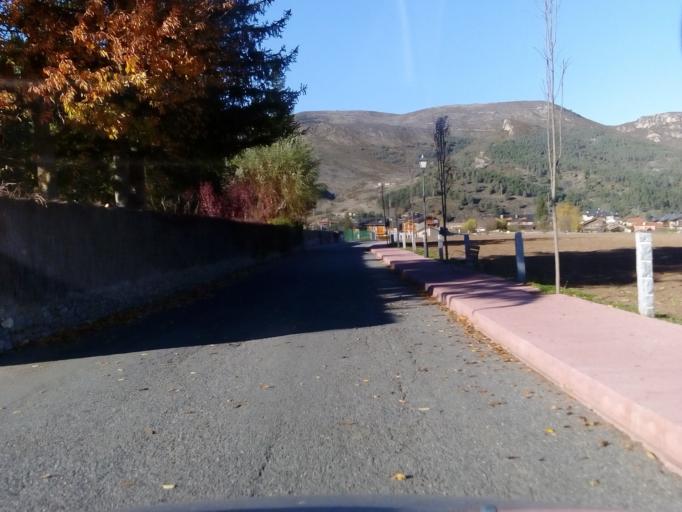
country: ES
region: Catalonia
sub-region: Provincia de Lleida
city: Bellver de Cerdanya
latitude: 42.3652
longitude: 1.7786
